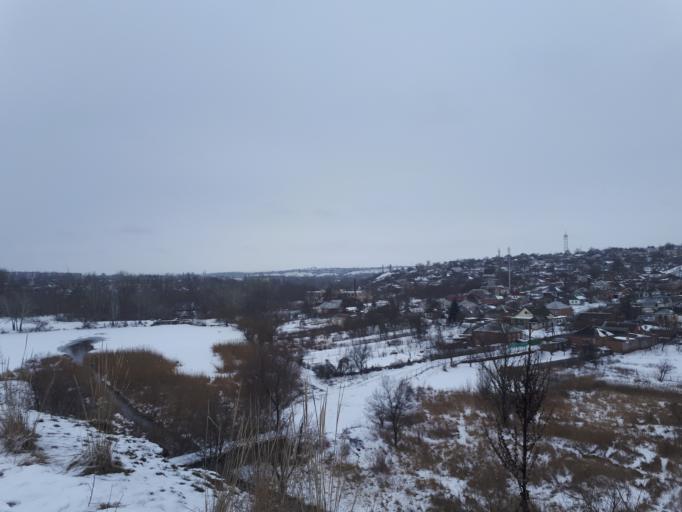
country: RU
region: Rostov
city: Krasnyy Sulin
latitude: 47.9055
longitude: 40.0445
